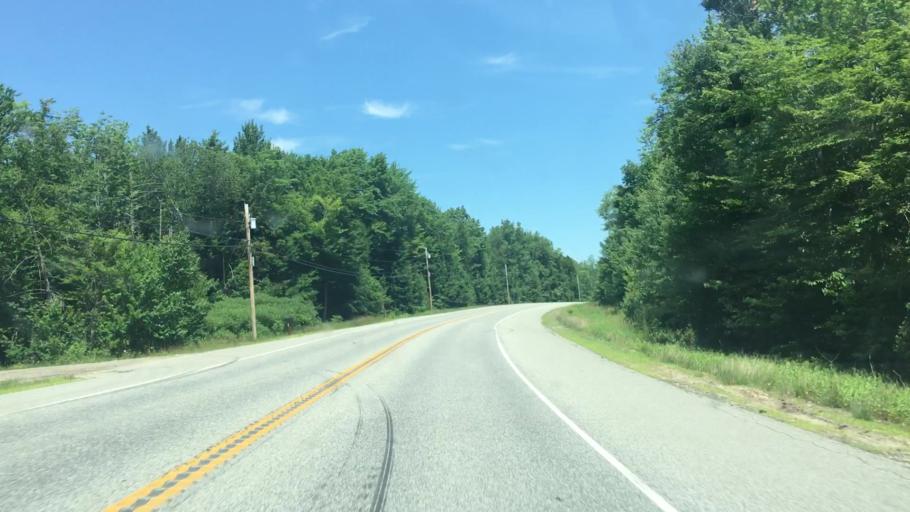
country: US
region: Maine
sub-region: Androscoggin County
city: Livermore
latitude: 44.4224
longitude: -70.2202
